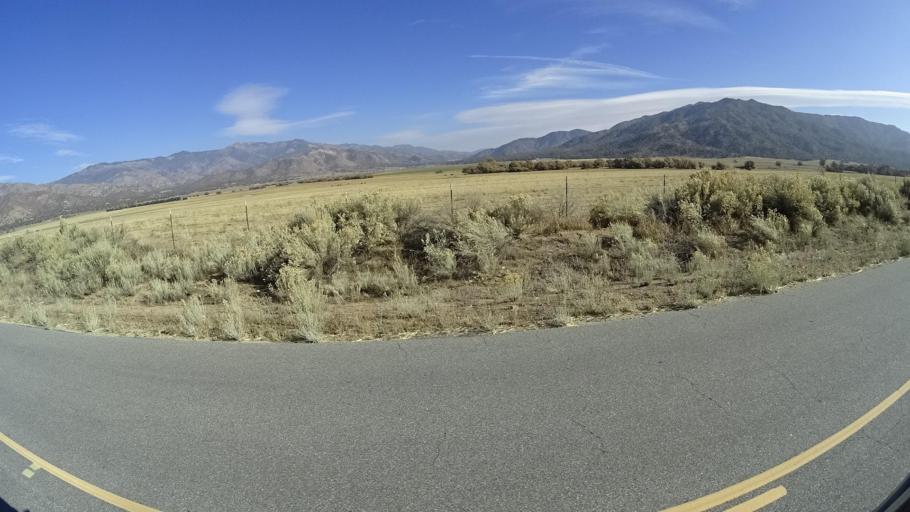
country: US
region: California
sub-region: Kern County
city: Bodfish
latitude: 35.4069
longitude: -118.5470
